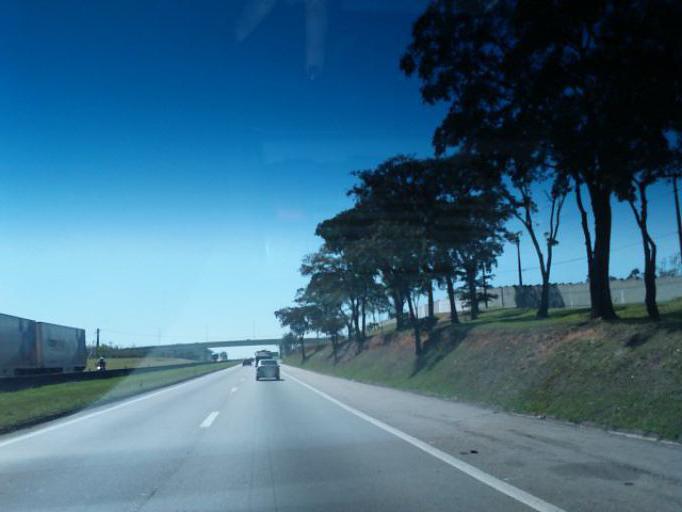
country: BR
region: Sao Paulo
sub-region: Sao Jose Dos Campos
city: Sao Jose dos Campos
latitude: -23.1632
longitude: -45.8073
